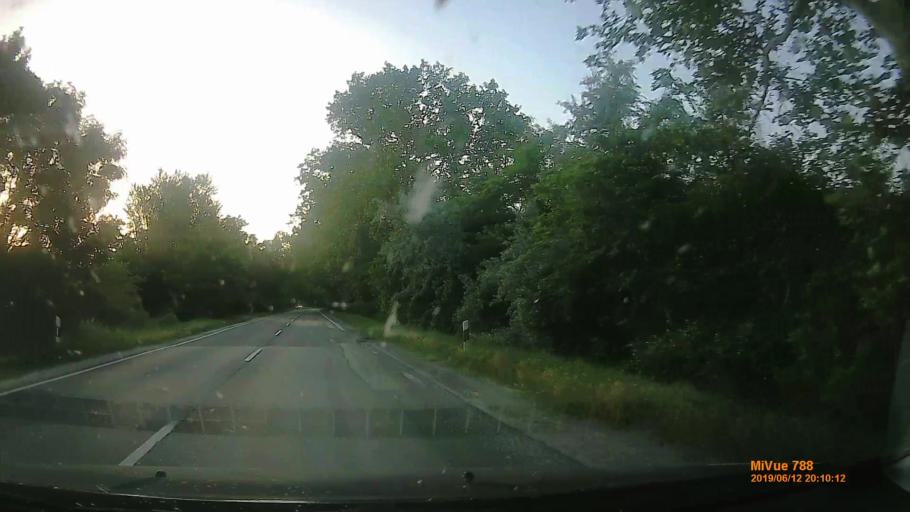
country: HU
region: Pest
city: Ocsa
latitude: 47.2627
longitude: 19.2174
